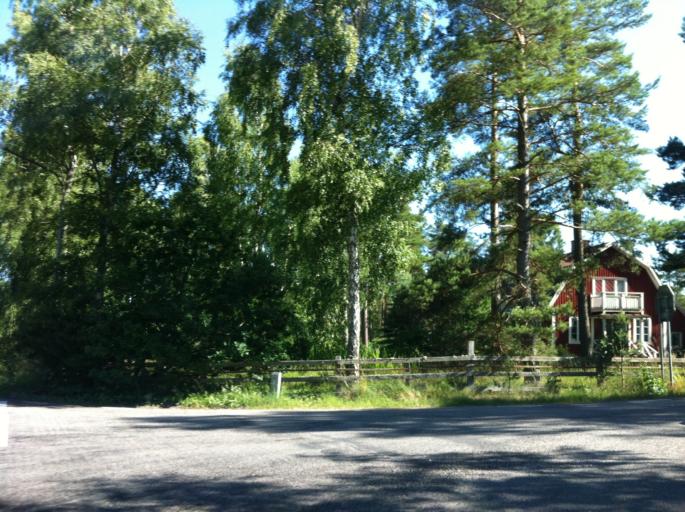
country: SE
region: Kalmar
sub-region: Borgholms Kommun
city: Borgholm
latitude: 57.2942
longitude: 17.0209
